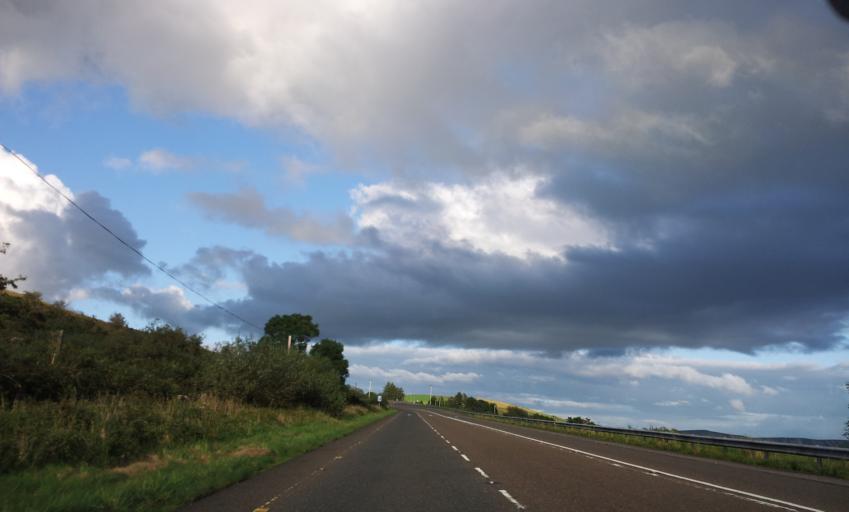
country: IE
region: Munster
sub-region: Ciarrai
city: Castleisland
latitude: 52.2648
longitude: -9.4344
